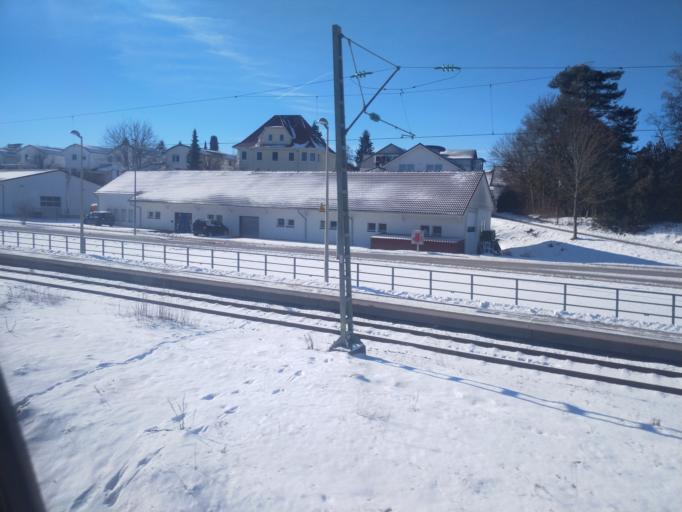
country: DE
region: Baden-Wuerttemberg
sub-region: Freiburg Region
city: Aldingen
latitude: 48.0954
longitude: 8.7146
